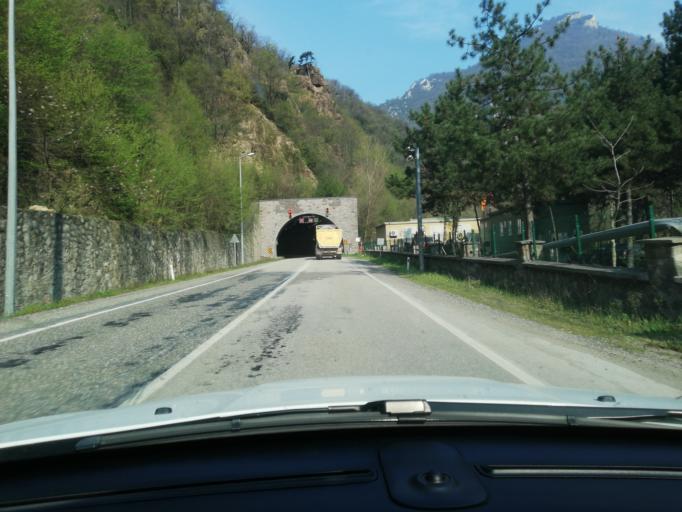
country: TR
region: Karabuk
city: Yenice
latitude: 41.1860
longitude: 32.4443
